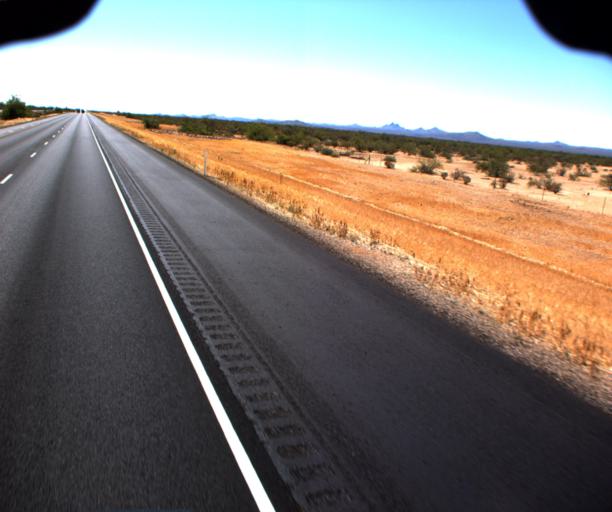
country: US
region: Arizona
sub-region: Yavapai County
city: Congress
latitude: 34.0847
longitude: -112.8955
